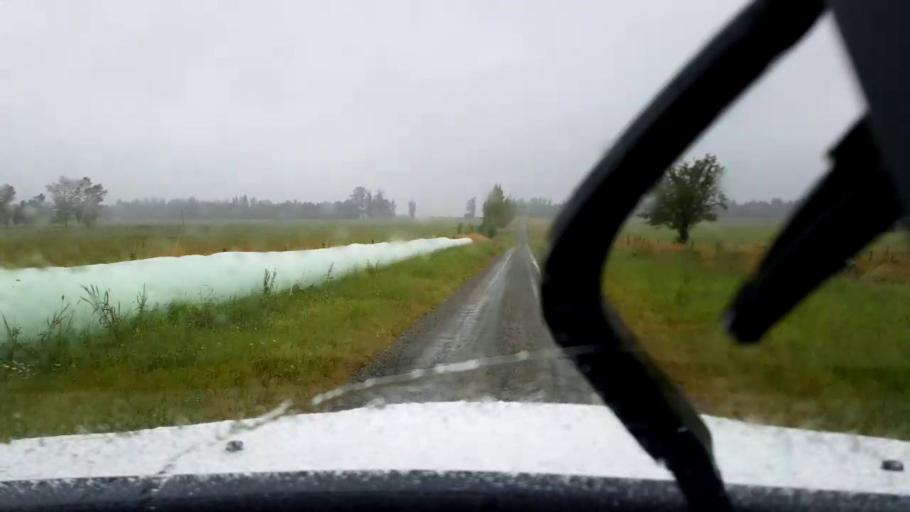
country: NZ
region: Canterbury
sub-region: Timaru District
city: Pleasant Point
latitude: -44.1976
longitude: 171.0910
